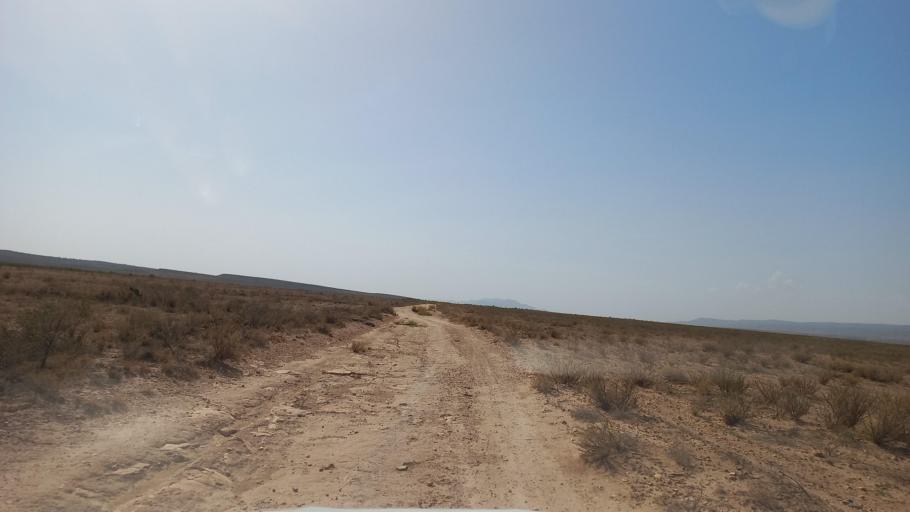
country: TN
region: Al Qasrayn
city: Kasserine
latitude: 35.2171
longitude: 9.0309
